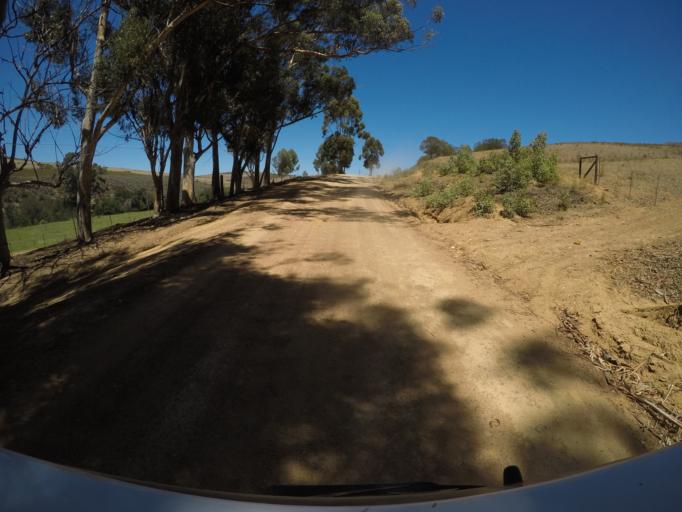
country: ZA
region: Western Cape
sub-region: Overberg District Municipality
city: Caledon
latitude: -34.2006
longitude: 19.2202
